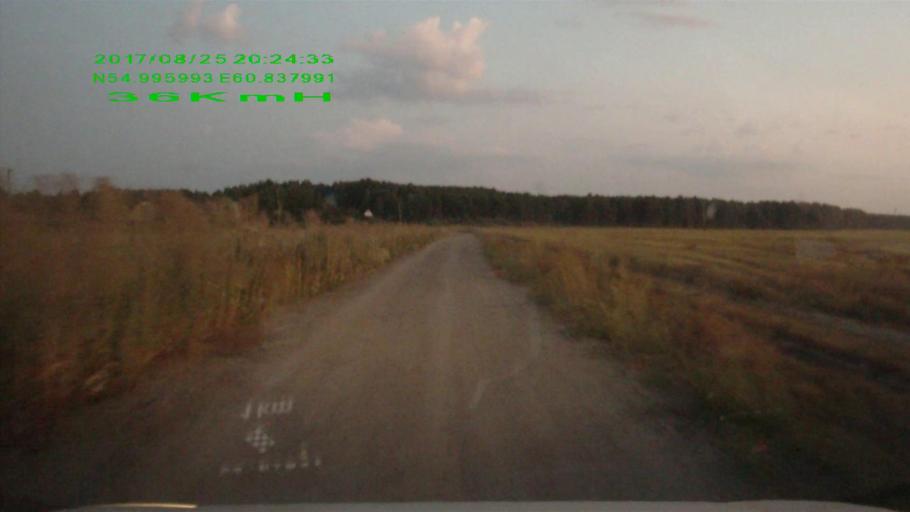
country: RU
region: Chelyabinsk
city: Timiryazevskiy
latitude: 54.9958
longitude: 60.8380
